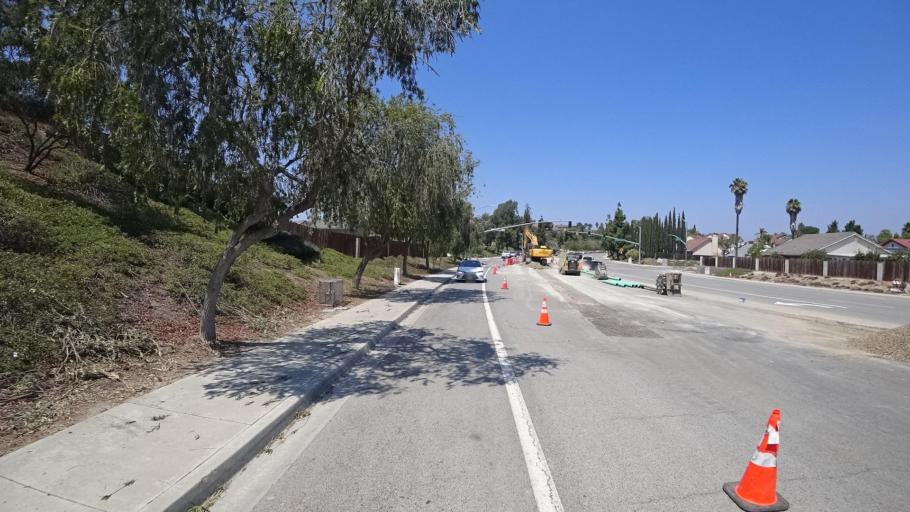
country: US
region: California
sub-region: San Diego County
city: Vista
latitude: 33.2229
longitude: -117.2627
